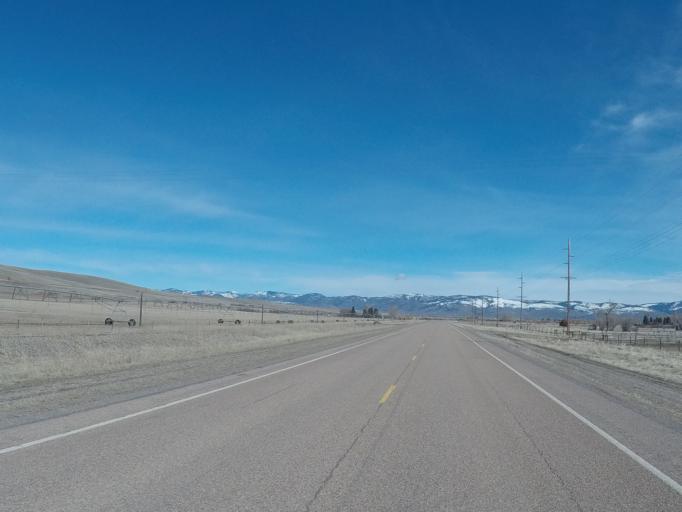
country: US
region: Montana
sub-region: Granite County
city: Philipsburg
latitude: 46.5477
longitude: -113.2186
